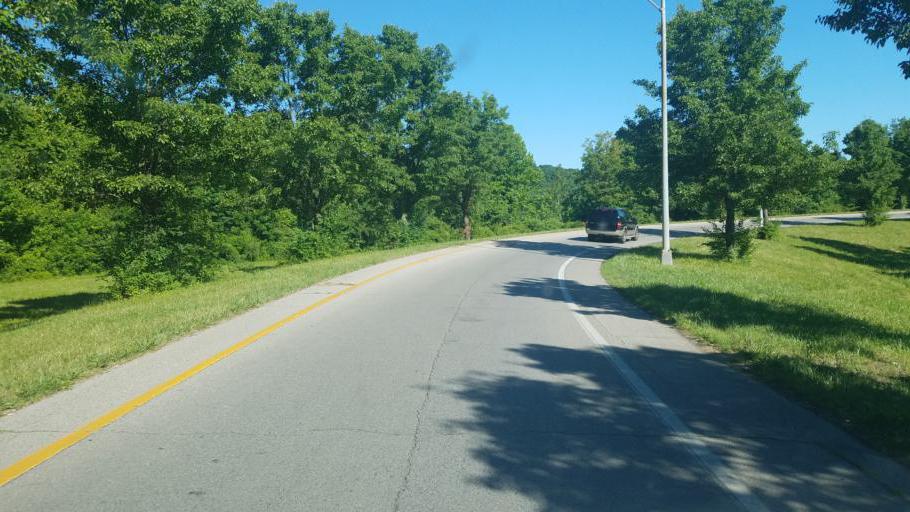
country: US
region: West Virginia
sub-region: Mason County
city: Point Pleasant
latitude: 38.8374
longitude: -82.1541
